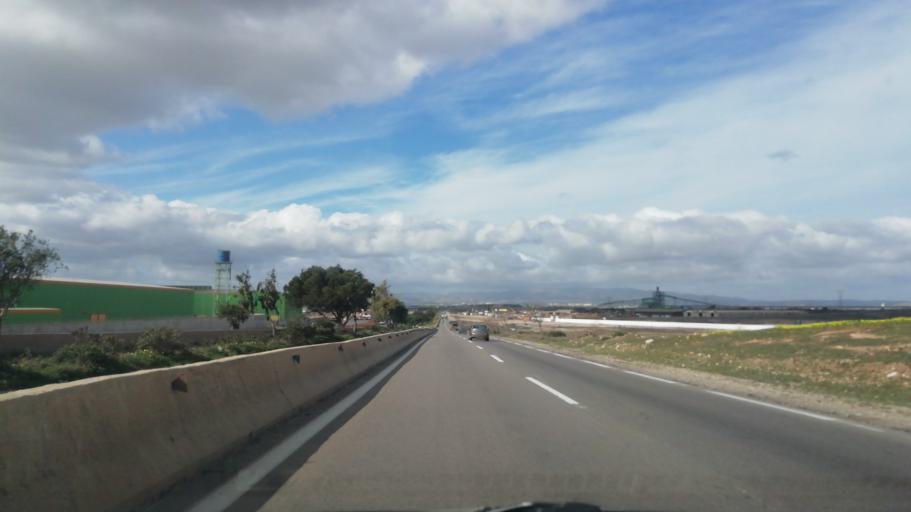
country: DZ
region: Oran
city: Ain el Bya
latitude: 35.7743
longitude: -0.2513
